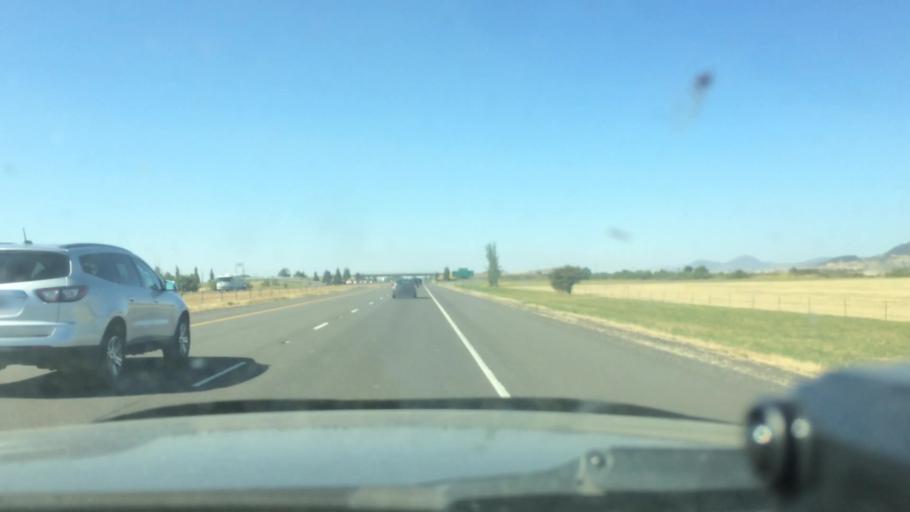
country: US
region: Oregon
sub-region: Linn County
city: Harrisburg
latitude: 44.2738
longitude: -123.0608
